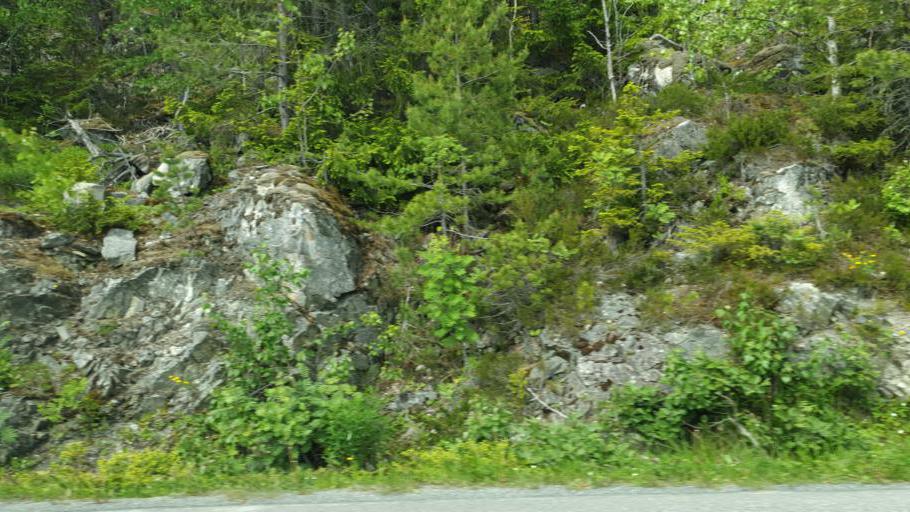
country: NO
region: Nord-Trondelag
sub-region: Leksvik
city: Leksvik
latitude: 63.6297
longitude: 10.5668
